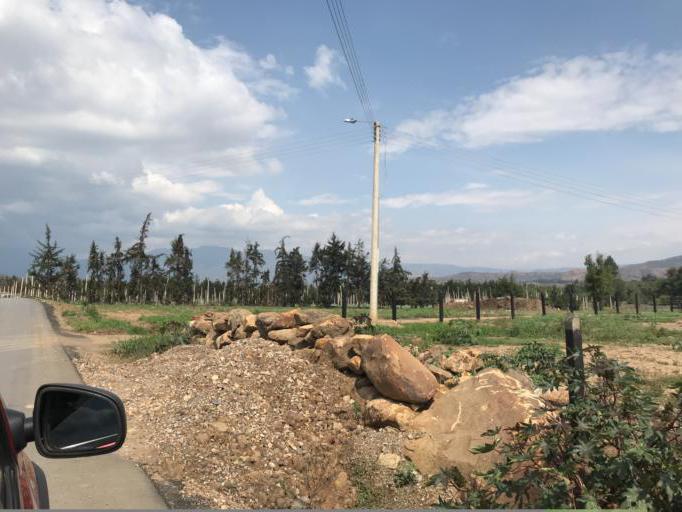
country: CO
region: Boyaca
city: Sutamarchan
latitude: 5.6303
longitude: -73.6087
